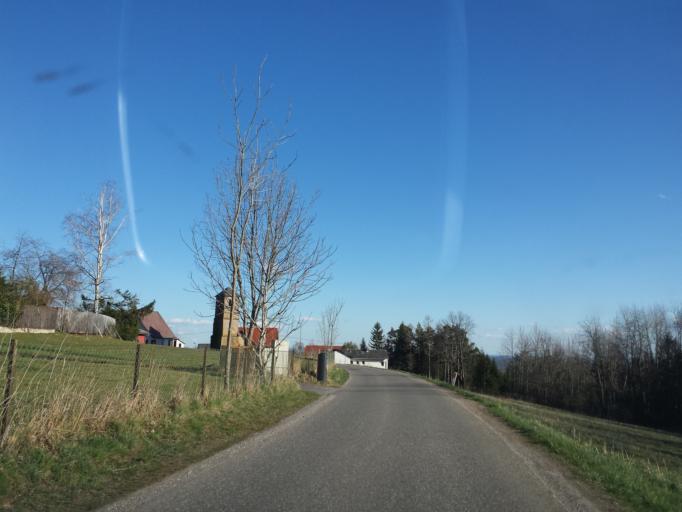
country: AT
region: Styria
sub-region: Politischer Bezirk Graz-Umgebung
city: Sankt Radegund bei Graz
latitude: 47.1639
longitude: 15.4830
